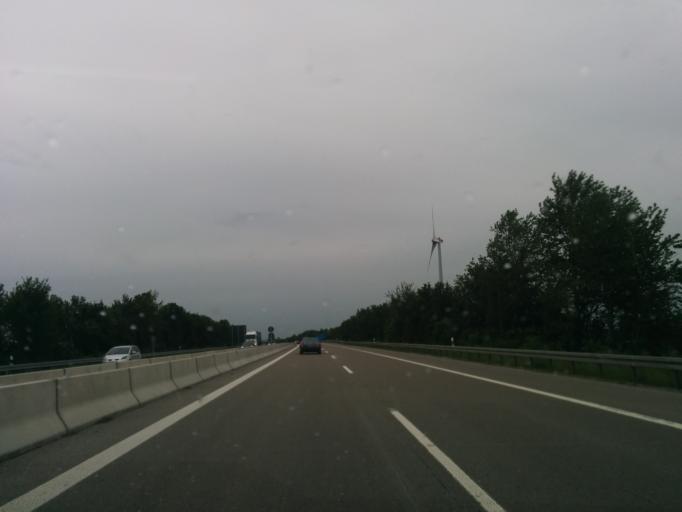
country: DE
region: Bavaria
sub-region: Regierungsbezirk Mittelfranken
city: Gollhofen
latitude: 49.5919
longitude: 10.1740
